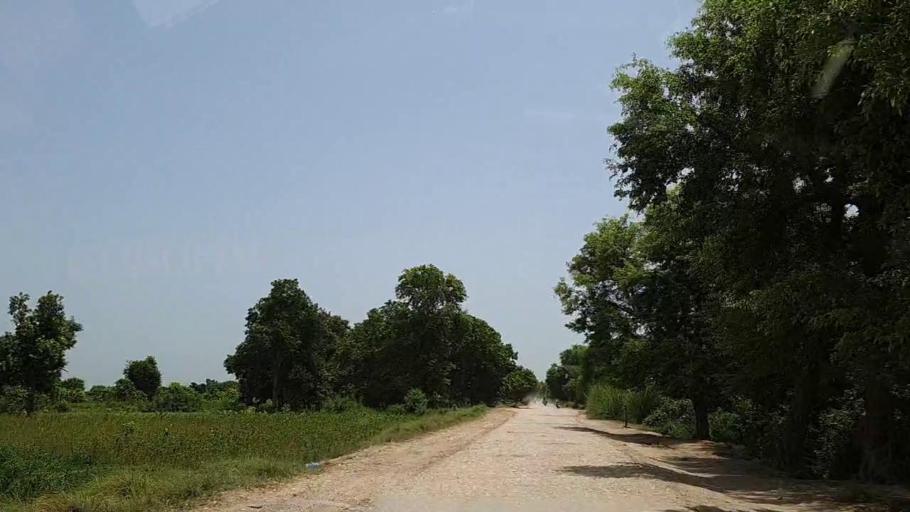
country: PK
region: Sindh
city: Tharu Shah
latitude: 26.9488
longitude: 68.0994
